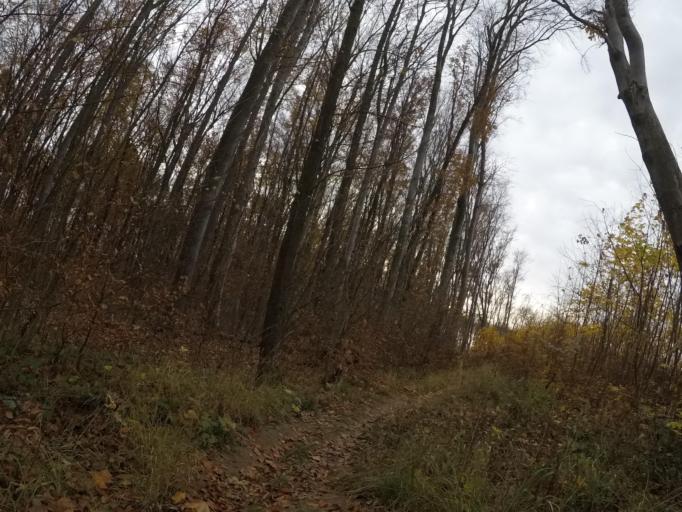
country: SK
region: Presovsky
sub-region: Okres Presov
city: Presov
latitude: 48.9685
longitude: 21.2085
